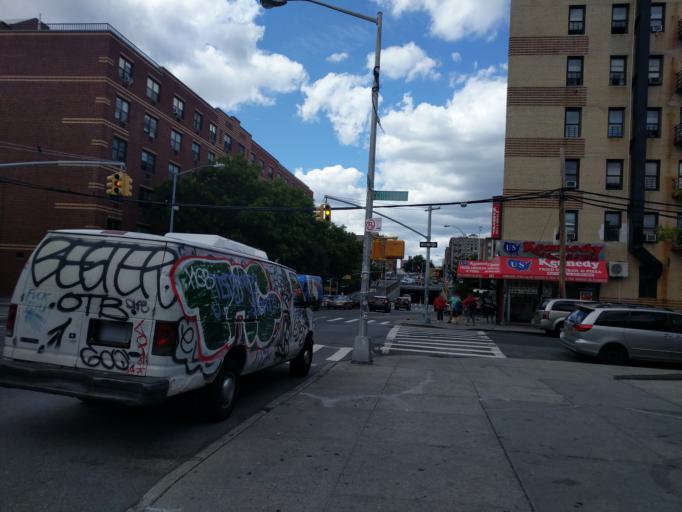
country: US
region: New York
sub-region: New York County
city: Inwood
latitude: 40.8375
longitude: -73.9104
